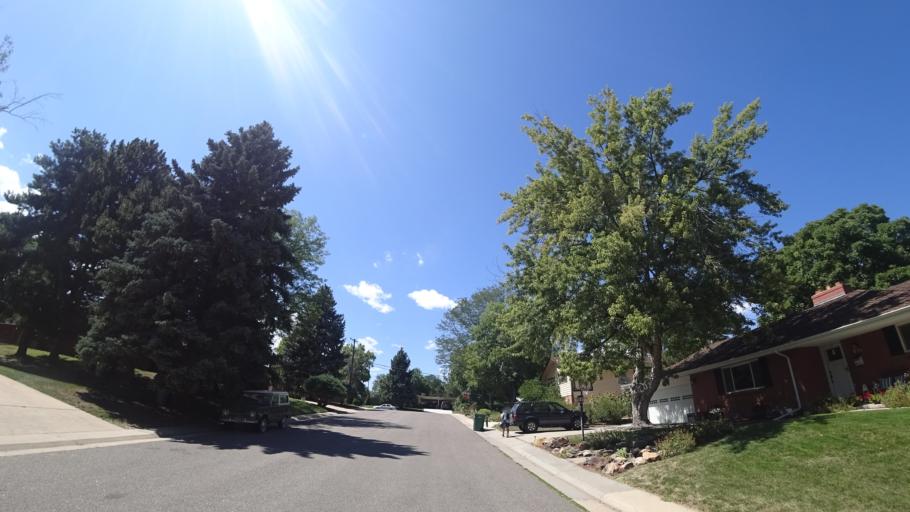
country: US
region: Colorado
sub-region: Arapahoe County
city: Greenwood Village
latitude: 39.6088
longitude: -104.9780
